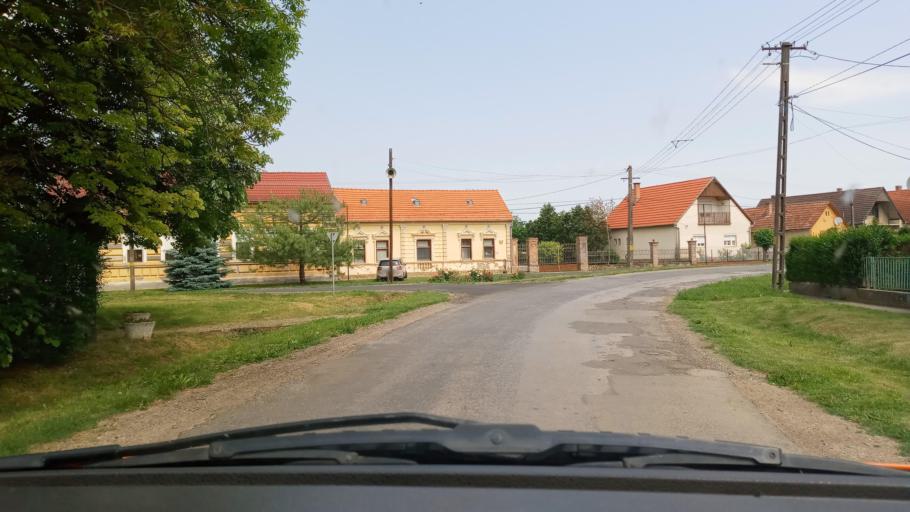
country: HU
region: Baranya
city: Szentlorinc
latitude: 46.0066
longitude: 18.0384
